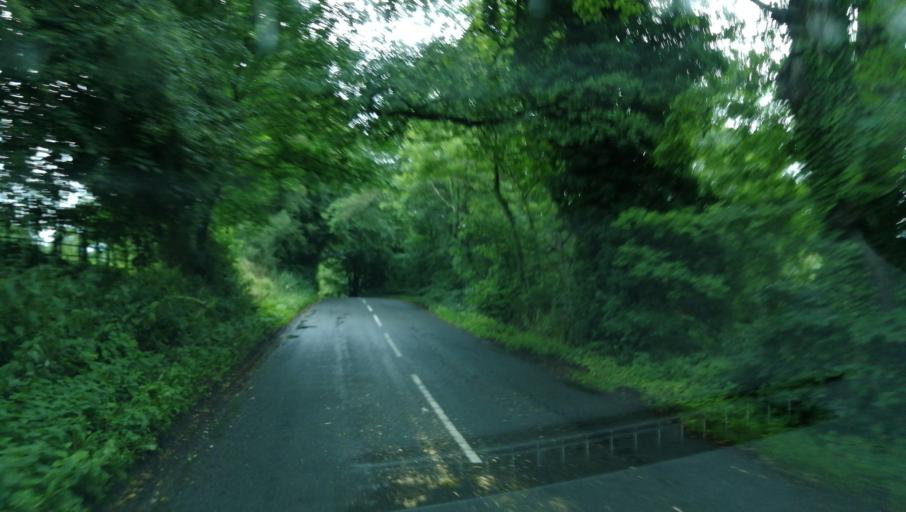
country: GB
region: England
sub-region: Cumbria
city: Penrith
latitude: 54.6368
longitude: -2.8012
